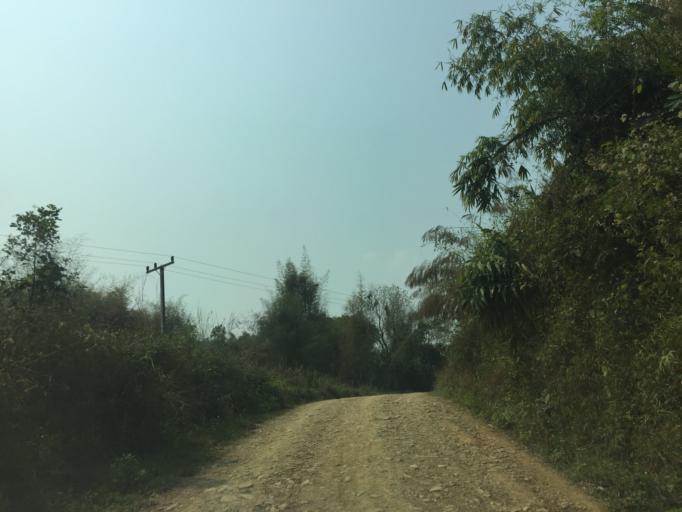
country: TH
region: Phayao
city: Phu Sang
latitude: 19.5979
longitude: 100.5320
